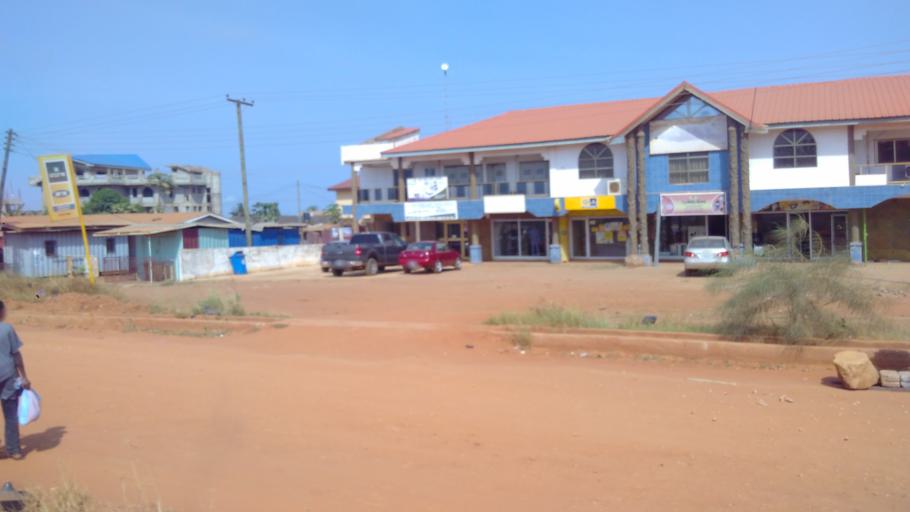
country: GH
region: Greater Accra
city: Nungua
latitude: 5.6339
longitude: -0.0645
